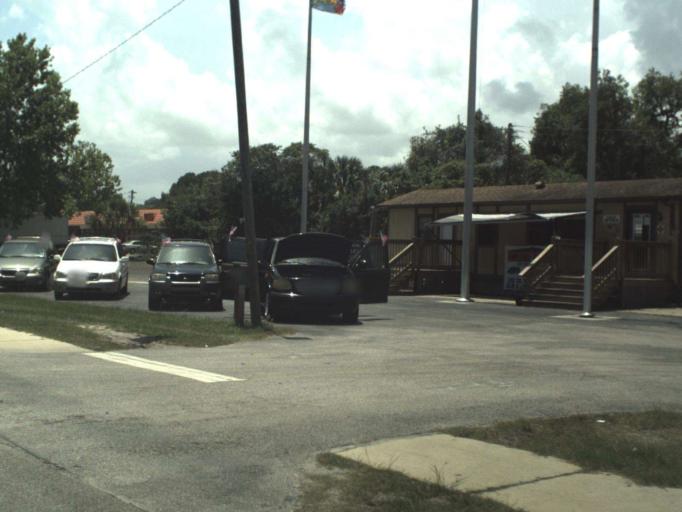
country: US
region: Florida
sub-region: Volusia County
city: Port Orange
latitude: 29.1096
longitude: -80.9734
